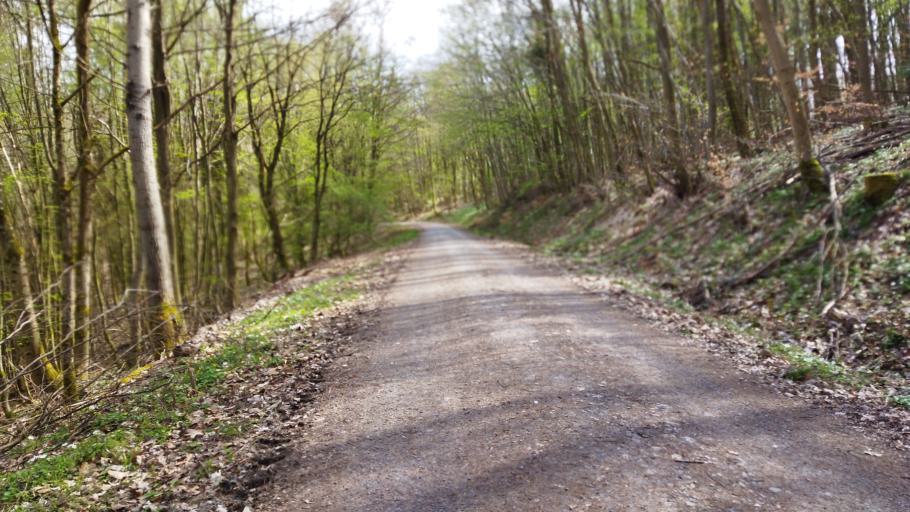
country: DE
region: Baden-Wuerttemberg
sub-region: Regierungsbezirk Stuttgart
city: Erlenbach
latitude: 49.1998
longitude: 9.2907
